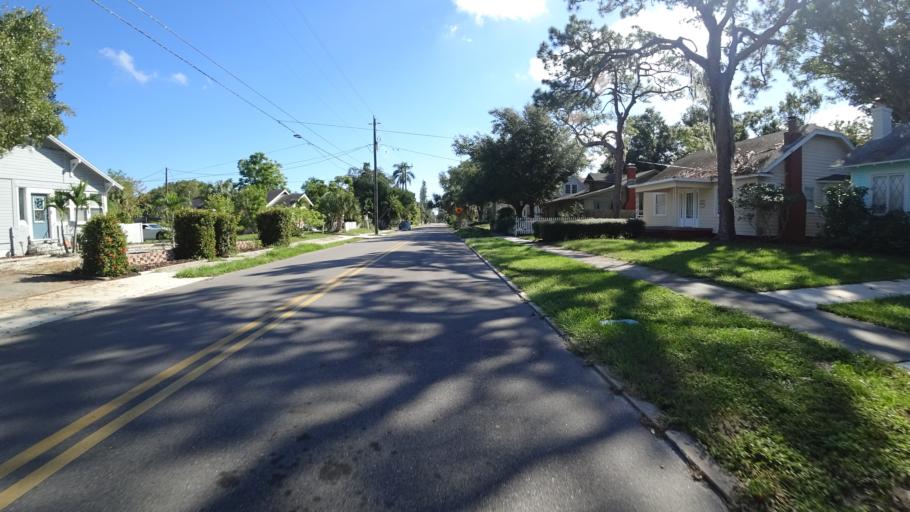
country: US
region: Florida
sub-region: Manatee County
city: Bradenton
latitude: 27.4937
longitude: -82.5847
